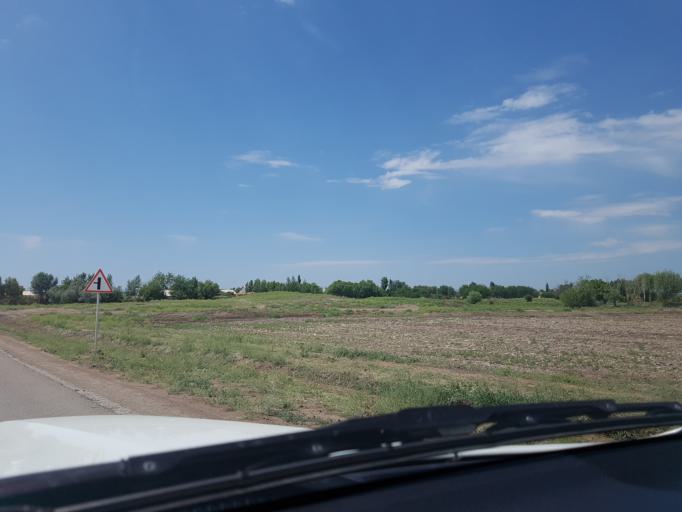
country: TM
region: Dasoguz
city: Koeneuergench
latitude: 42.3183
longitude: 59.1396
